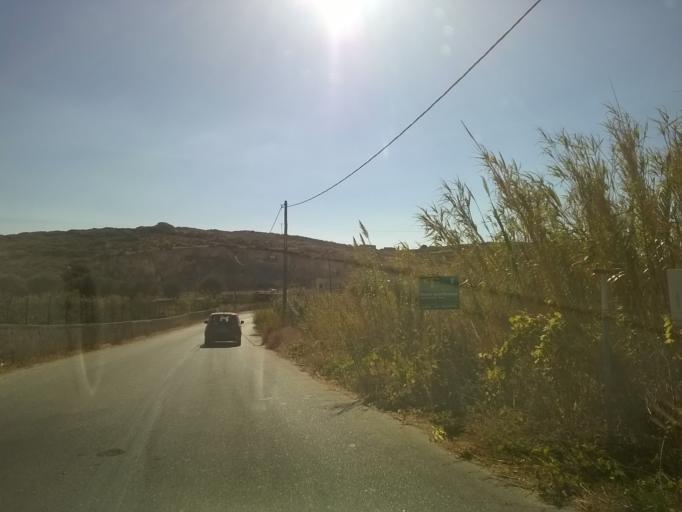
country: GR
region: South Aegean
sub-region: Nomos Kykladon
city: Naxos
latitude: 37.0437
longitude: 25.4104
